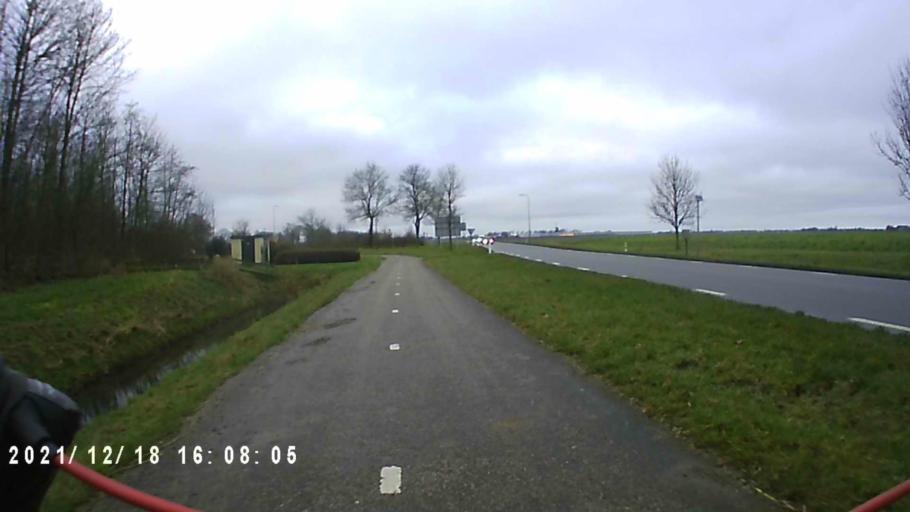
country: NL
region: Friesland
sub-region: Gemeente Dongeradeel
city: Anjum
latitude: 53.3588
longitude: 6.0742
